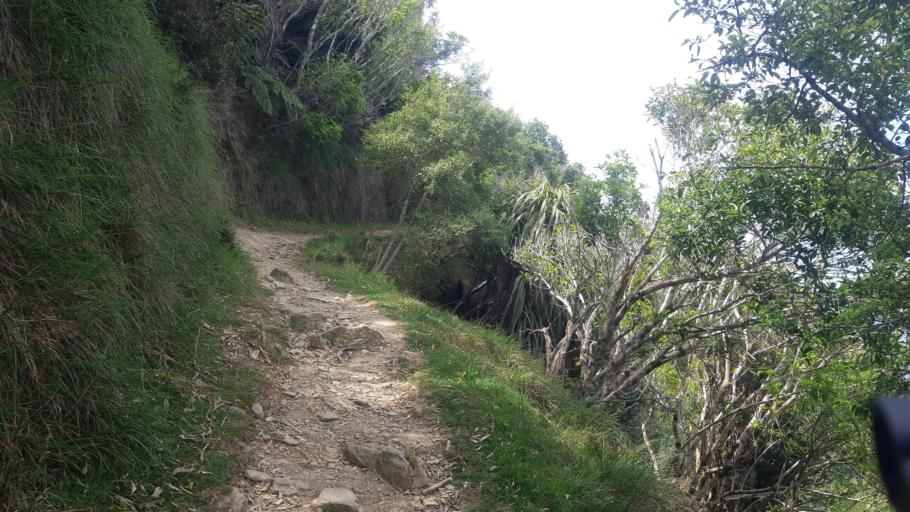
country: NZ
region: Marlborough
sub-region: Marlborough District
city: Picton
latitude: -41.2502
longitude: 173.9608
